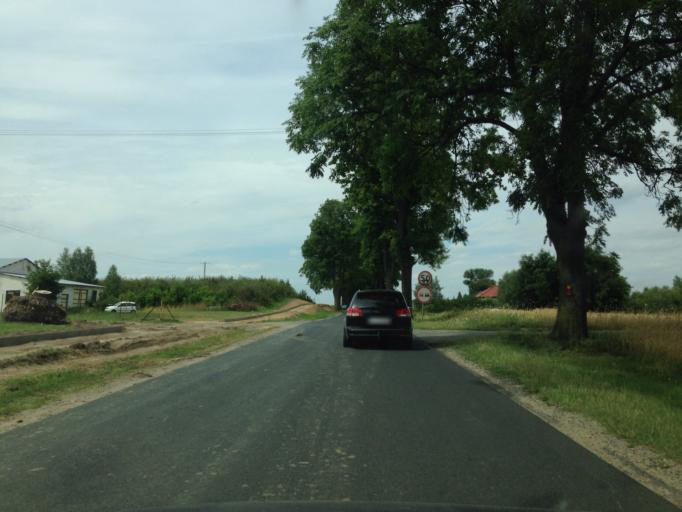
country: PL
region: Kujawsko-Pomorskie
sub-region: Powiat brodnicki
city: Brodnica
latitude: 53.3062
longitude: 19.3947
